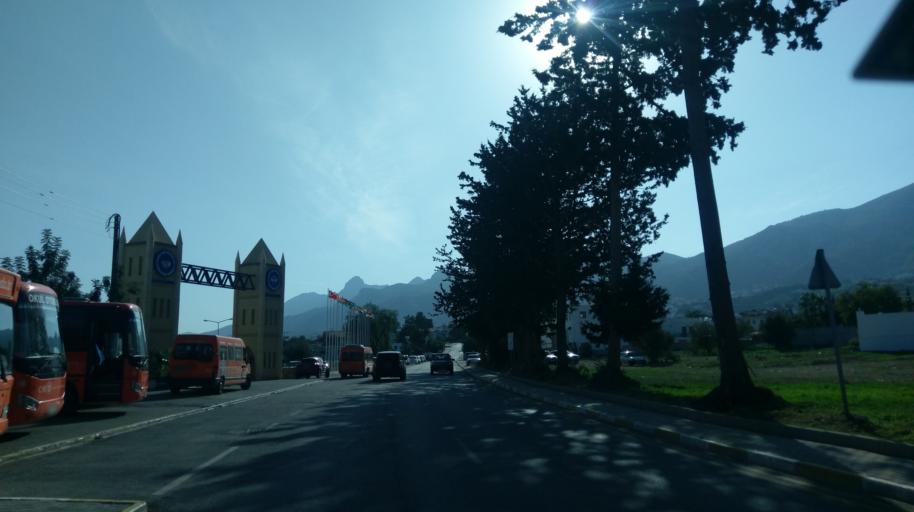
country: CY
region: Keryneia
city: Kyrenia
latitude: 35.3249
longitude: 33.3441
